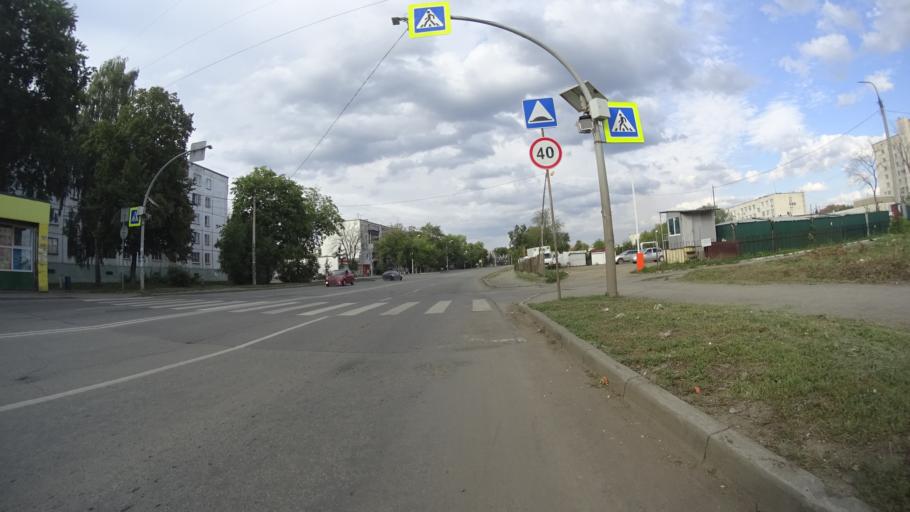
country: RU
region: Chelyabinsk
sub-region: Gorod Chelyabinsk
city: Chelyabinsk
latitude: 55.2007
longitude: 61.3198
